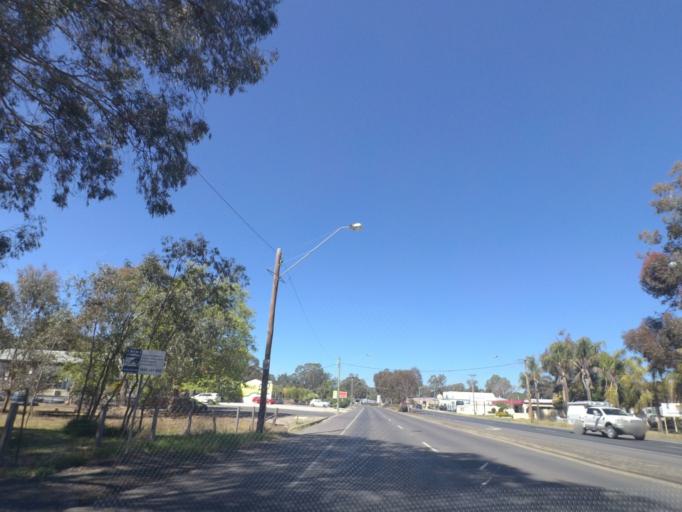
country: AU
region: Victoria
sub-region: Murrindindi
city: Kinglake West
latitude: -37.0214
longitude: 145.1214
